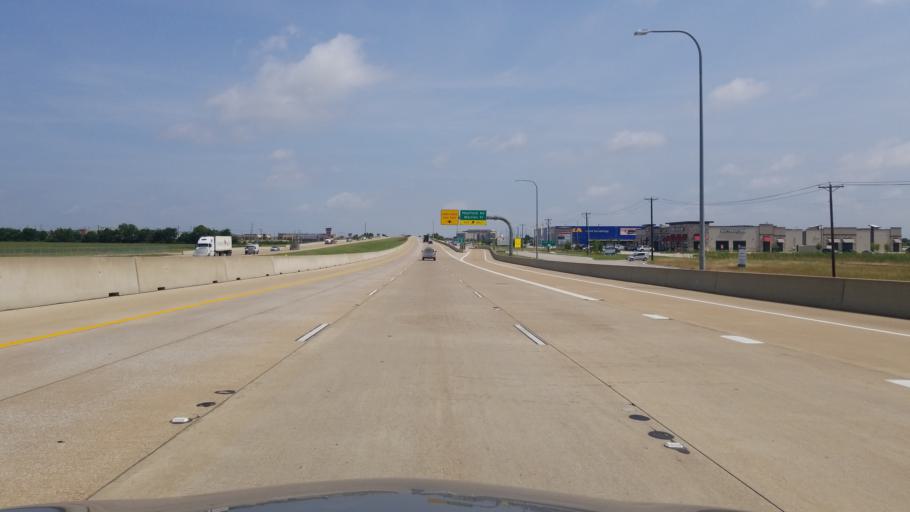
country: US
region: Texas
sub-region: Dallas County
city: Grand Prairie
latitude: 32.6856
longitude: -97.0240
